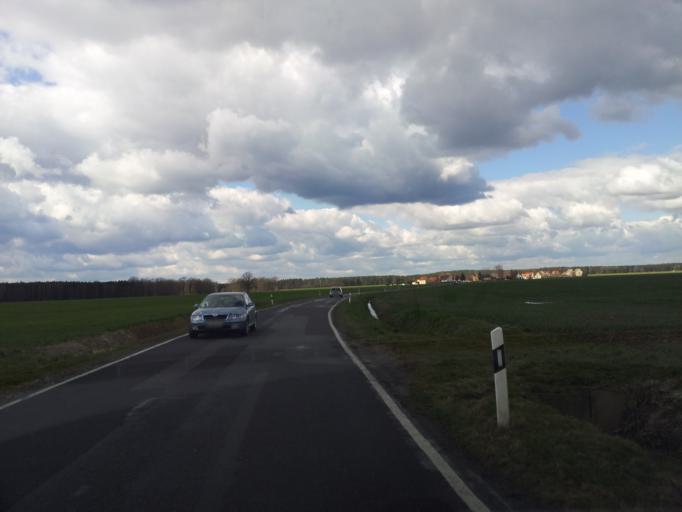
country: DE
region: Saxony
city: Horka
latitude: 51.2941
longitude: 14.2230
